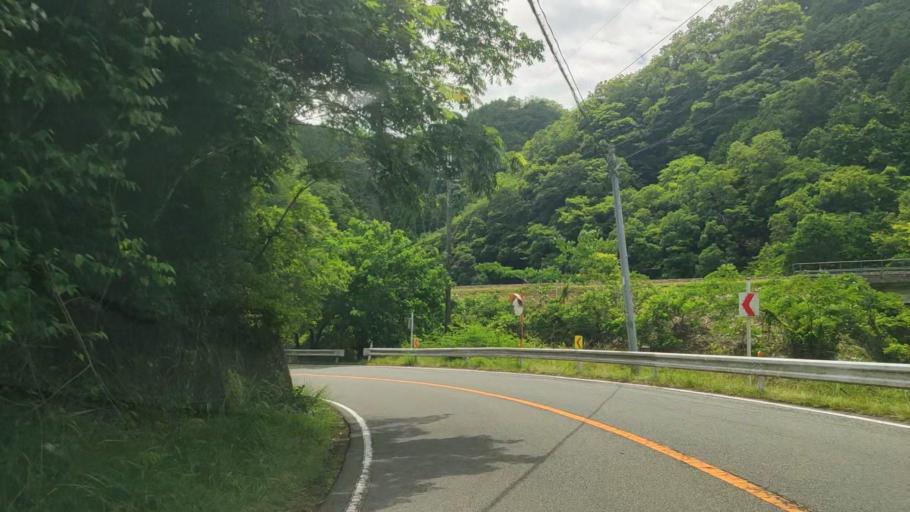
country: JP
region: Hyogo
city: Yamazakicho-nakabirose
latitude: 35.0782
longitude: 134.3591
